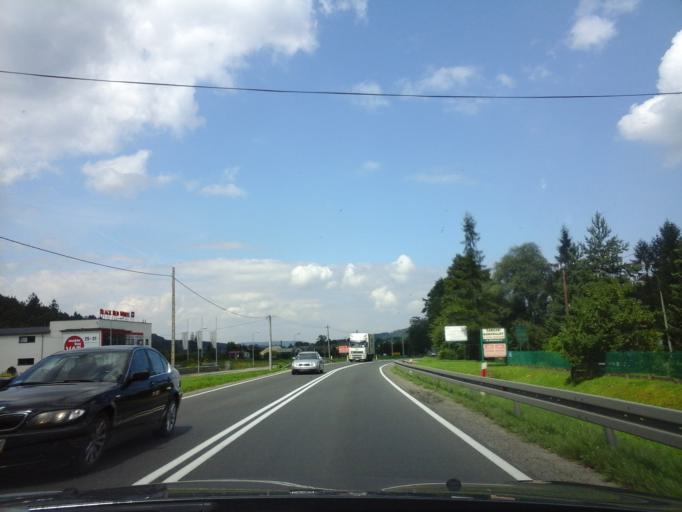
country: PL
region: Lesser Poland Voivodeship
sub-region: Powiat suski
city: Sucha Beskidzka
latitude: 49.7532
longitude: 19.6045
